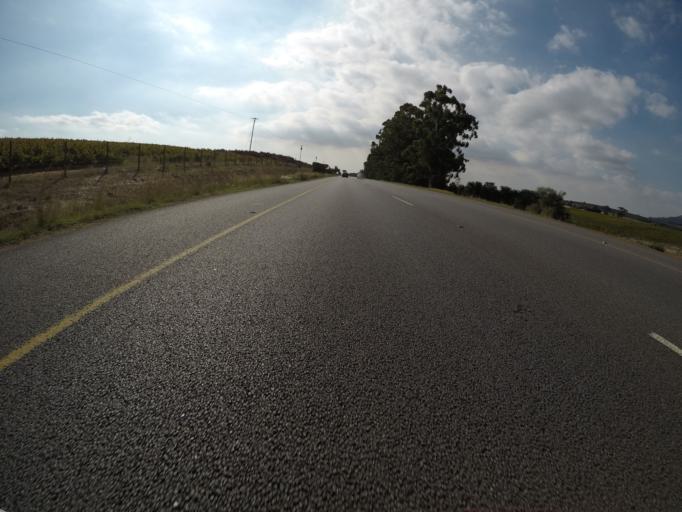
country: ZA
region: Western Cape
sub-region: Cape Winelands District Municipality
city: Stellenbosch
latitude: -33.8868
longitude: 18.8224
